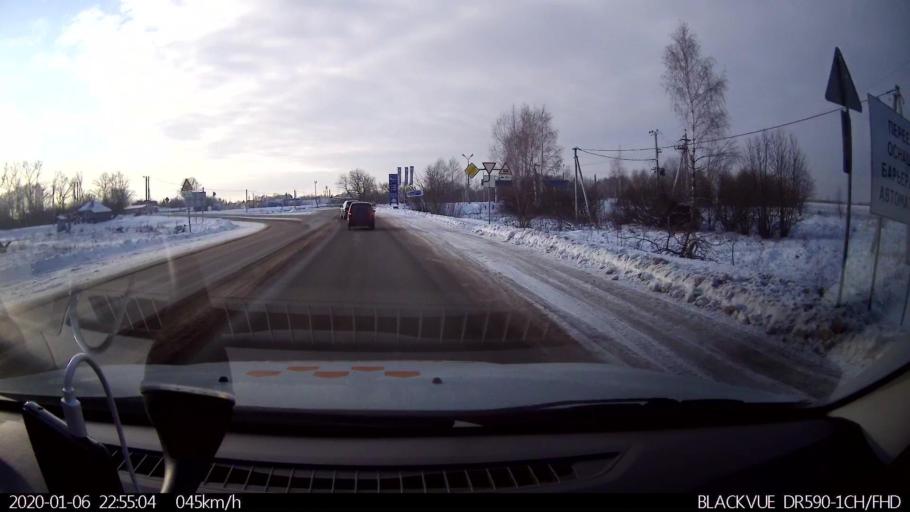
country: RU
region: Nizjnij Novgorod
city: Bogorodsk
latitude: 56.1171
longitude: 43.5422
